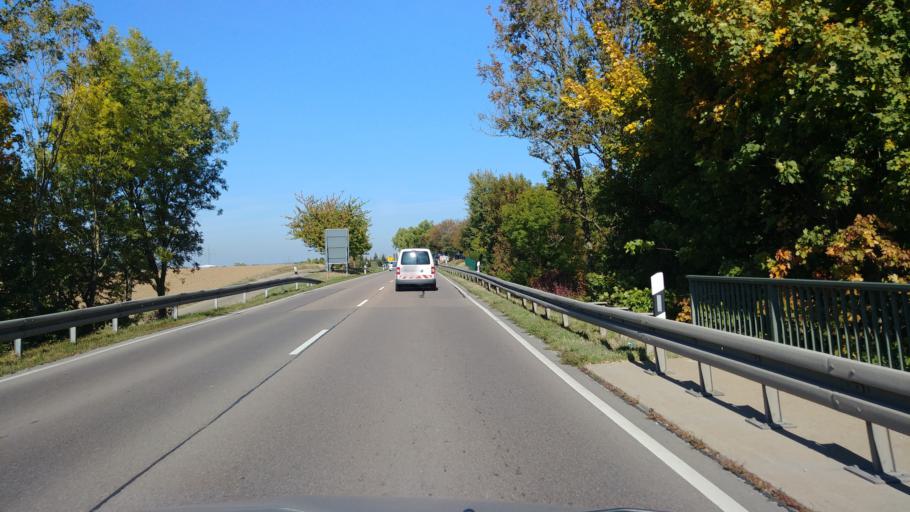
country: DE
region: Baden-Wuerttemberg
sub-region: Regierungsbezirk Stuttgart
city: Untermunkheim
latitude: 49.1727
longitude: 9.7129
